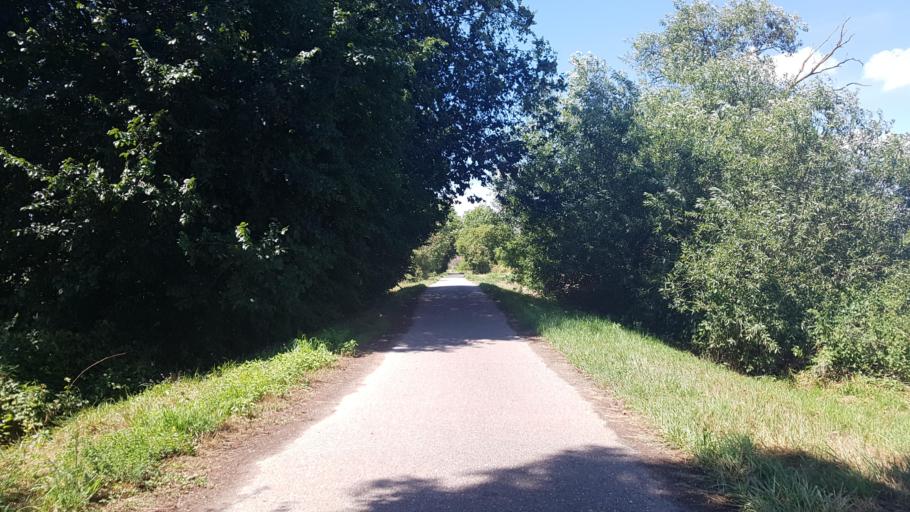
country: FR
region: Lorraine
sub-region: Departement de Meurthe-et-Moselle
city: Laneuveville-devant-Nancy
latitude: 48.6617
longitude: 6.2350
